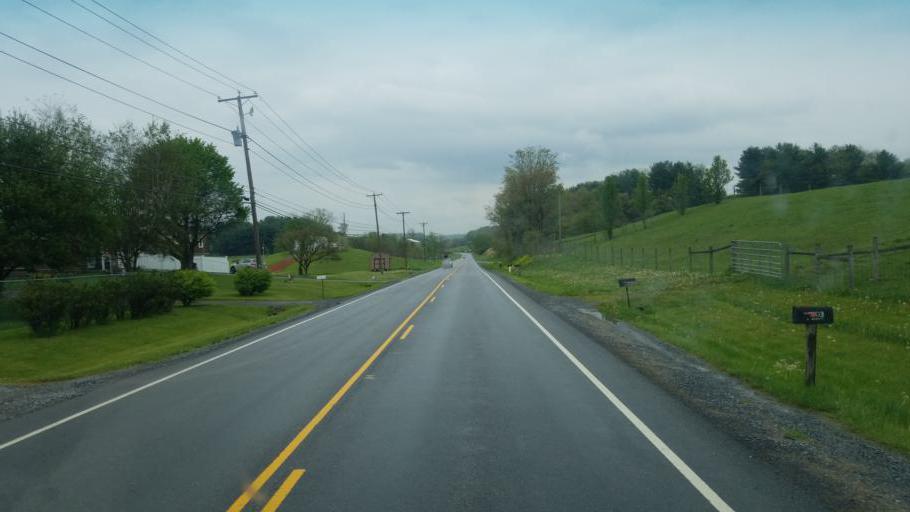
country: US
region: Virginia
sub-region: Smyth County
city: Atkins
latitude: 36.8890
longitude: -81.3583
